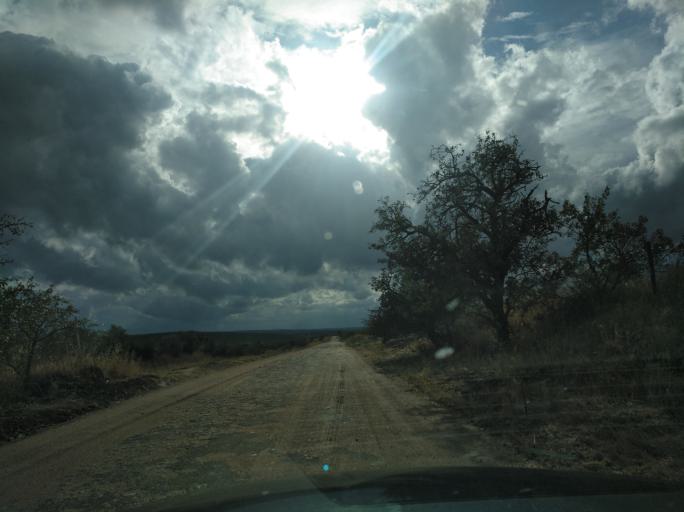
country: PT
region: Portalegre
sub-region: Campo Maior
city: Campo Maior
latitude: 39.0400
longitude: -7.1104
